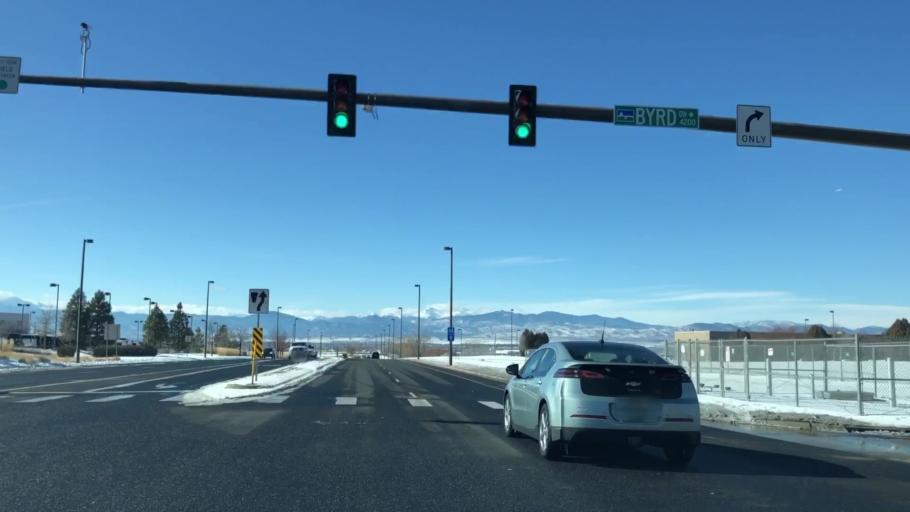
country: US
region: Colorado
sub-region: Larimer County
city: Loveland
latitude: 40.4370
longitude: -104.9977
